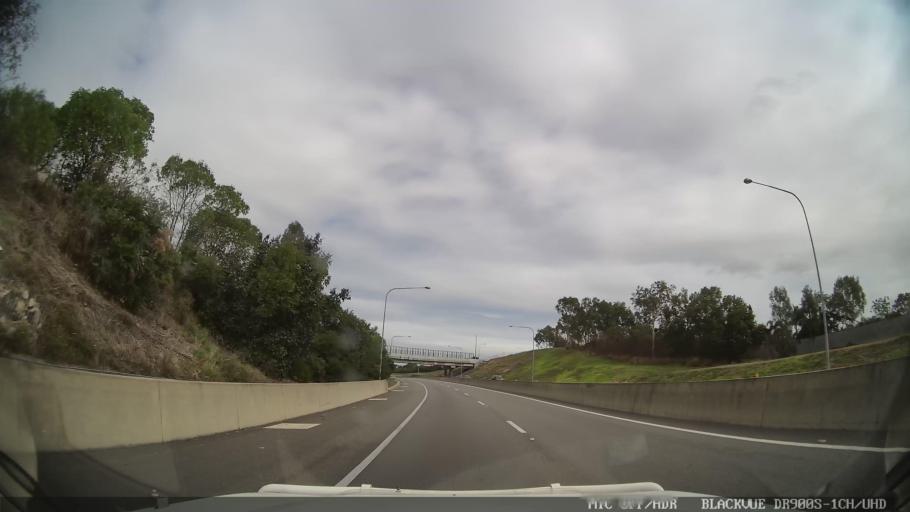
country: AU
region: Queensland
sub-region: Townsville
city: Bohle Plains
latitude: -19.3214
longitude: 146.7436
